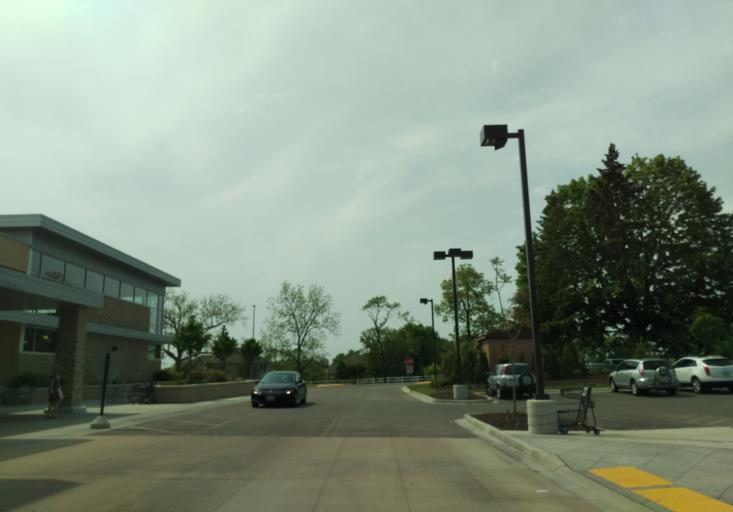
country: US
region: Wisconsin
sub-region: Dane County
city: Monona
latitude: 43.0853
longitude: -89.2765
